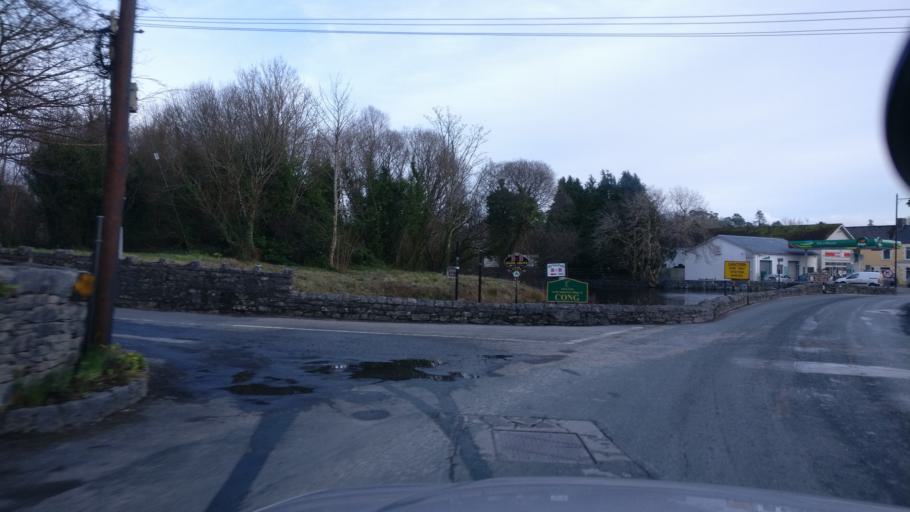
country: IE
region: Connaught
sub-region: Maigh Eo
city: Ballinrobe
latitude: 53.5431
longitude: -9.2877
